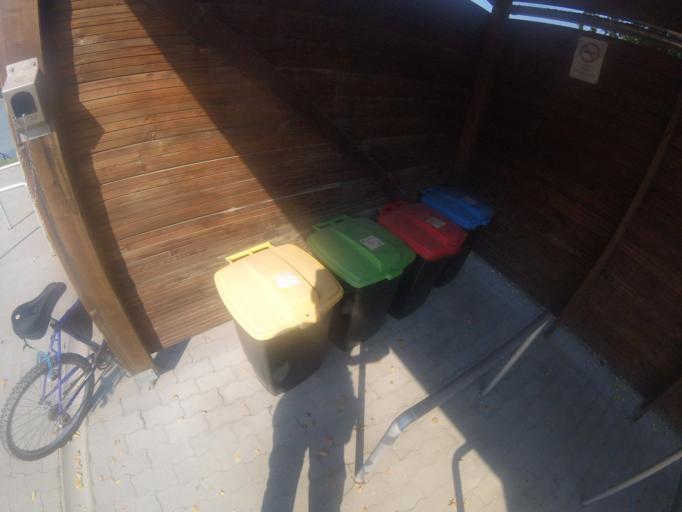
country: HU
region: Bacs-Kiskun
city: Baja
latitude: 46.1916
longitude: 18.9301
